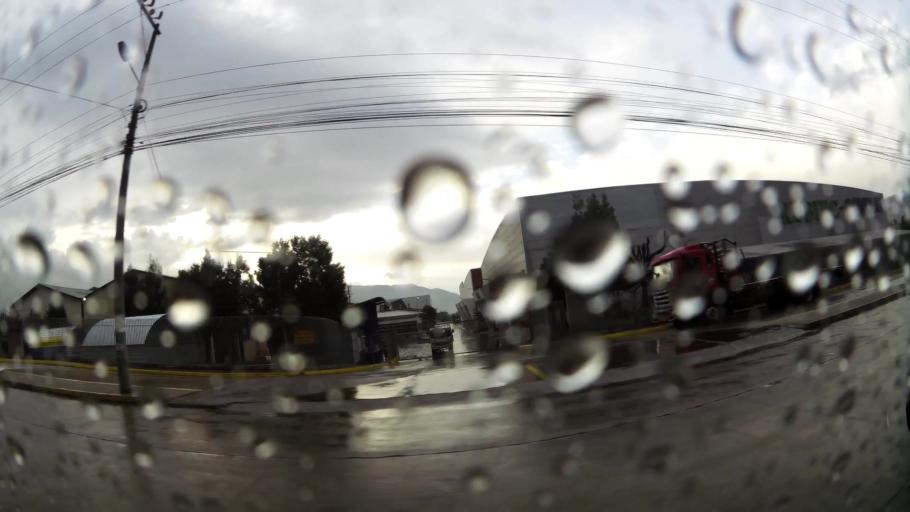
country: EC
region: Pichincha
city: Quito
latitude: -0.3035
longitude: -78.5470
